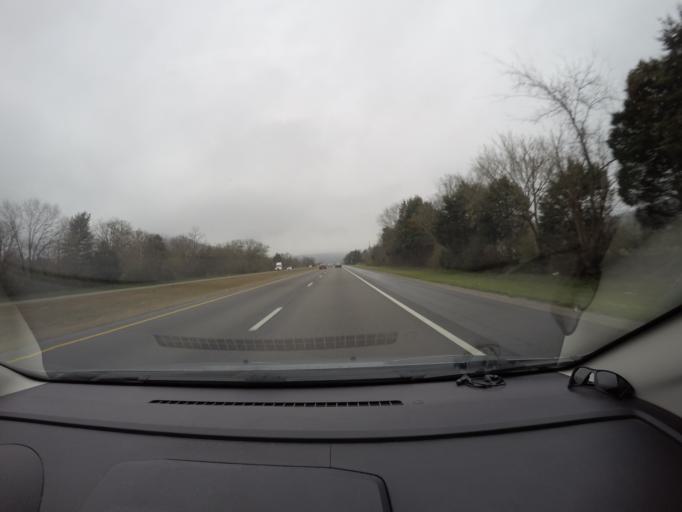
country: US
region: Tennessee
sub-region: Marion County
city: Kimball
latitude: 35.0831
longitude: -85.7367
